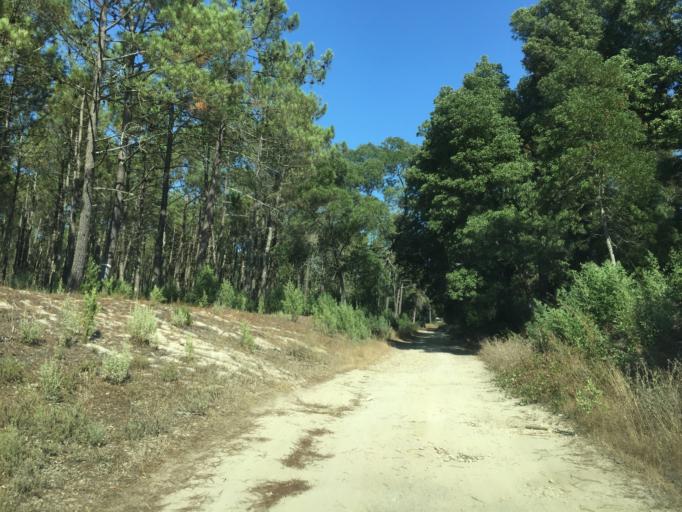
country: PT
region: Coimbra
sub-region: Figueira da Foz
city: Tavarede
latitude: 40.2273
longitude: -8.8505
